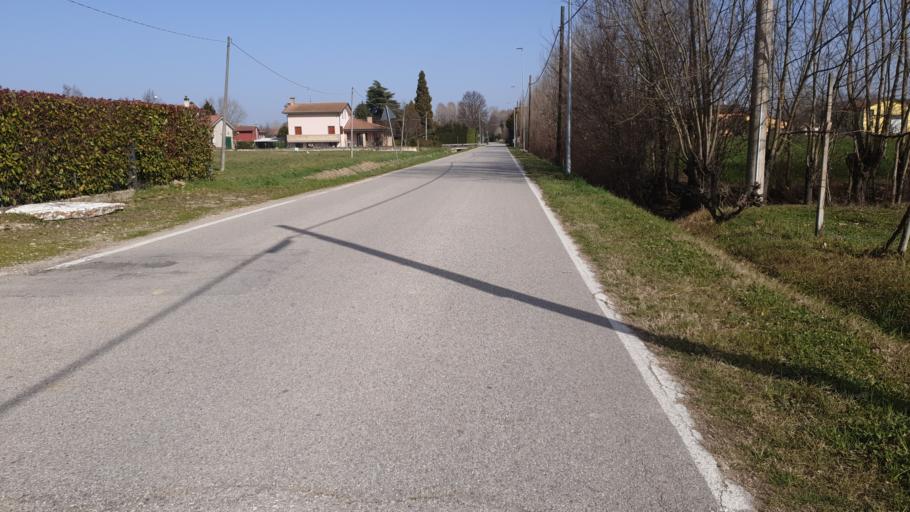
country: IT
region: Veneto
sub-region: Provincia di Padova
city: Cavino
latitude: 45.5182
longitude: 11.8994
